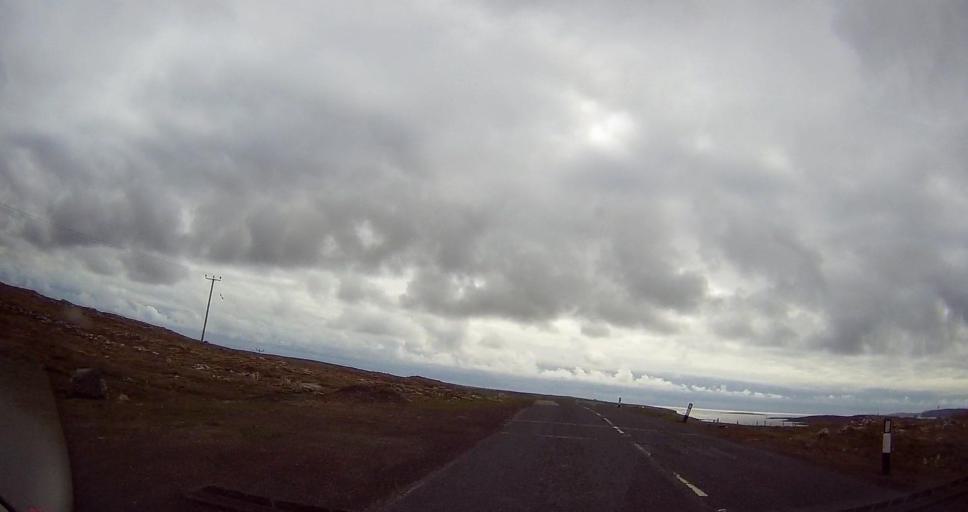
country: GB
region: Scotland
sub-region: Shetland Islands
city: Shetland
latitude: 60.6938
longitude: -0.9481
